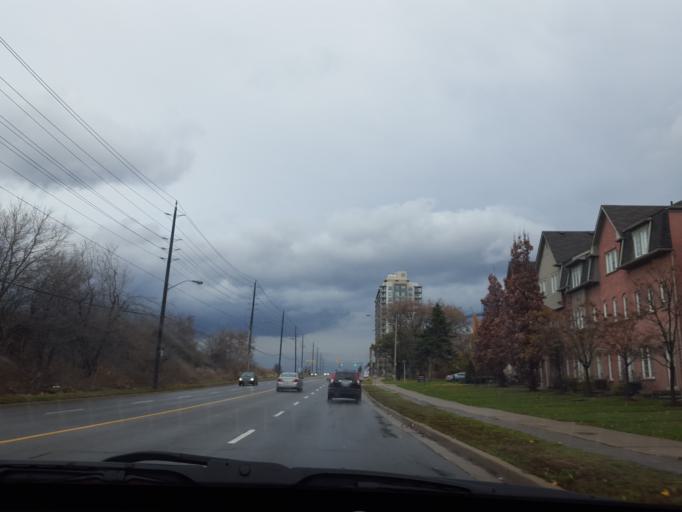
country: CA
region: Ontario
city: Ajax
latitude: 43.8256
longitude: -79.0960
